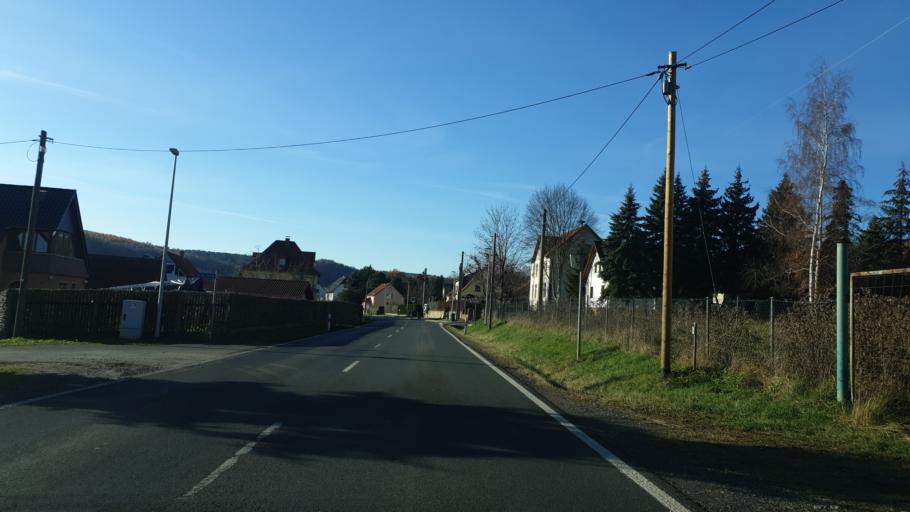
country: DE
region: Thuringia
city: Rauda
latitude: 50.9553
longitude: 11.9492
